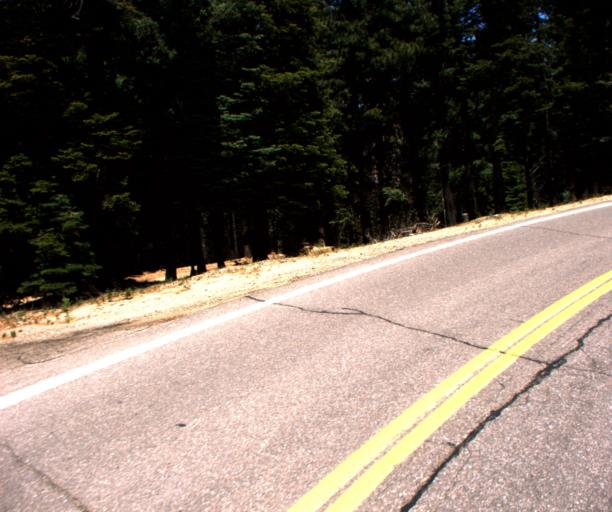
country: US
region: Arizona
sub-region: Graham County
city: Swift Trail Junction
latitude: 32.6491
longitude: -109.8624
